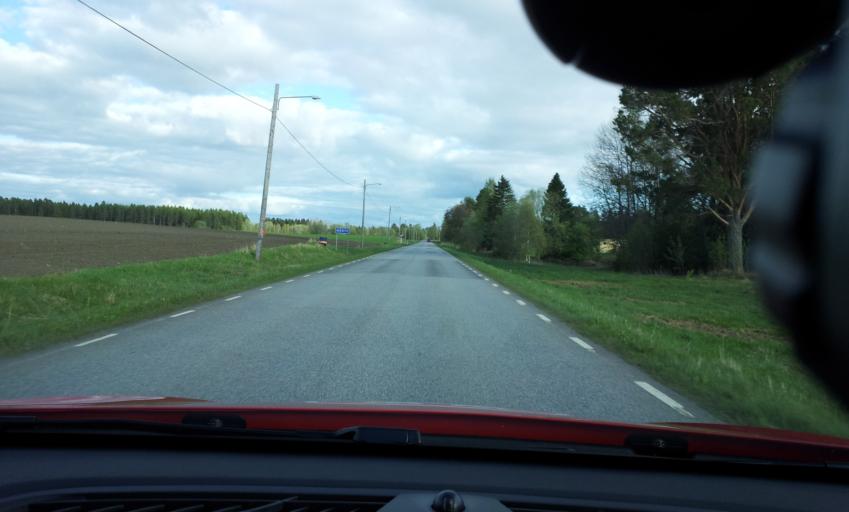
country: SE
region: Jaemtland
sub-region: Krokoms Kommun
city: Krokom
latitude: 63.2624
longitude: 14.3992
